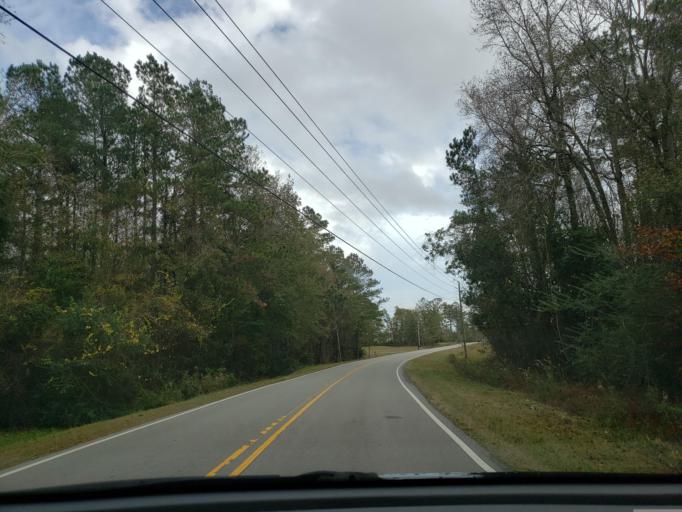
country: US
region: North Carolina
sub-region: Onslow County
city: Jacksonville
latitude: 34.7058
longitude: -77.5751
